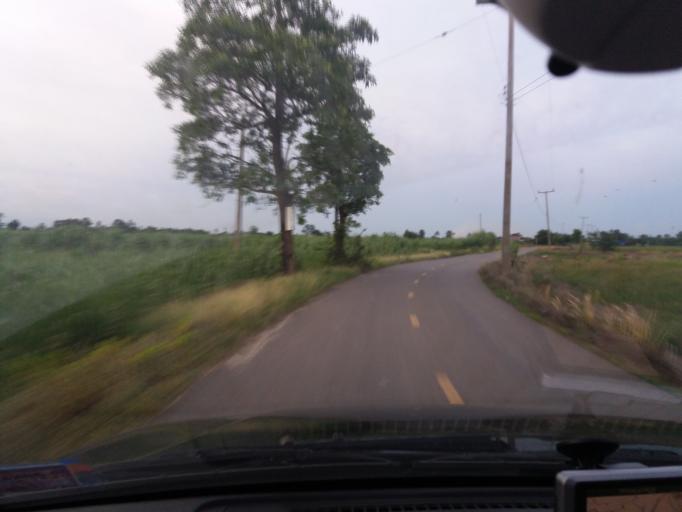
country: TH
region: Suphan Buri
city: Doembang Nangbuat
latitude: 14.8228
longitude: 100.1395
